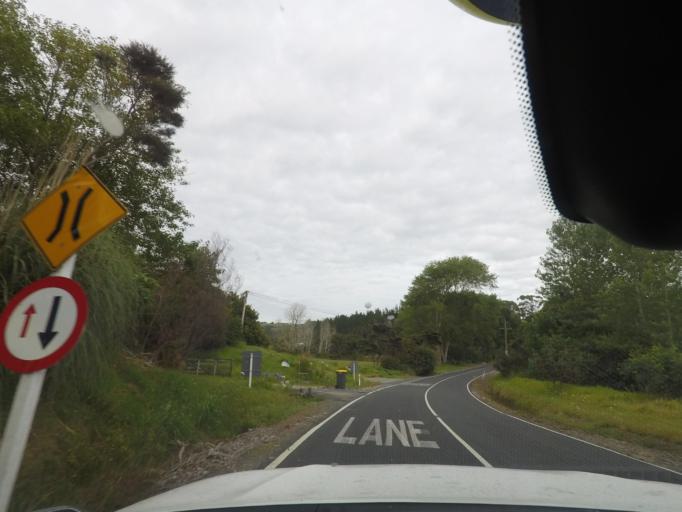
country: NZ
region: Auckland
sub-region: Auckland
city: Parakai
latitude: -36.5236
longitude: 174.2851
